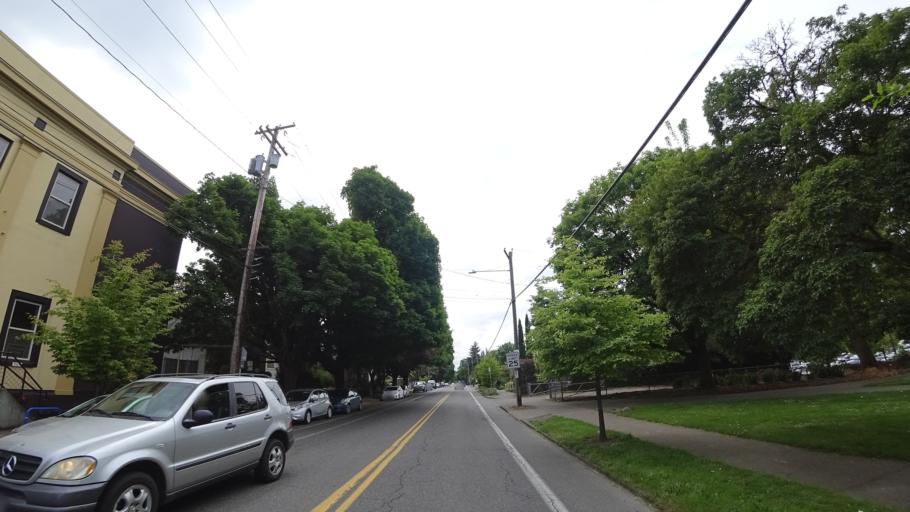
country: US
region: Oregon
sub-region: Multnomah County
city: Portland
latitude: 45.4974
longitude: -122.6397
